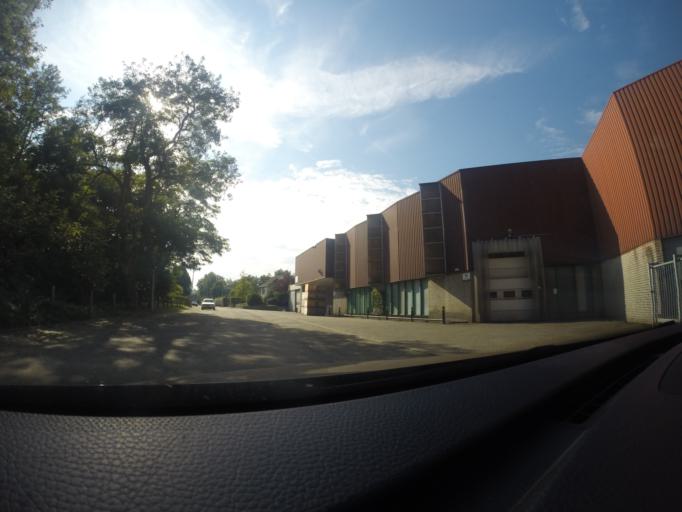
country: NL
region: Gelderland
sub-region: Oude IJsselstreek
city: Wisch
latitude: 51.9316
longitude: 6.3557
